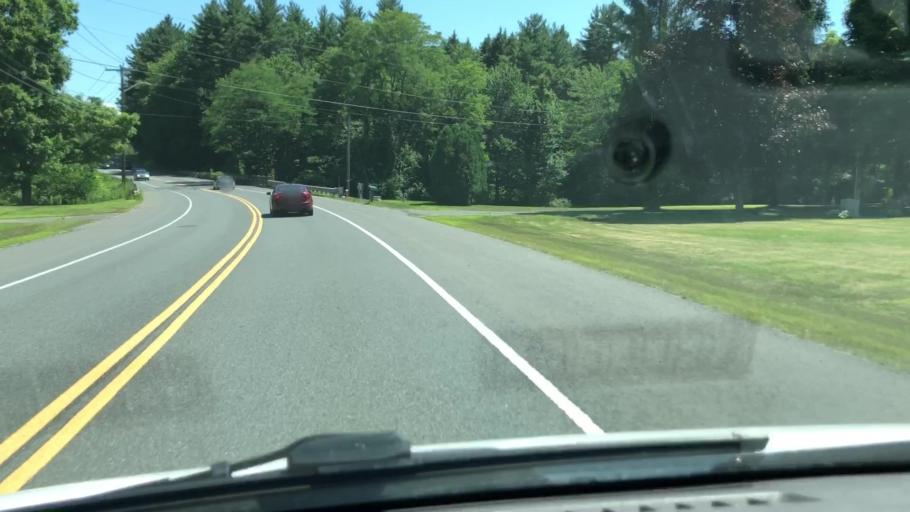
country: US
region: Massachusetts
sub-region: Hampshire County
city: Williamsburg
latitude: 42.3630
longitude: -72.6941
